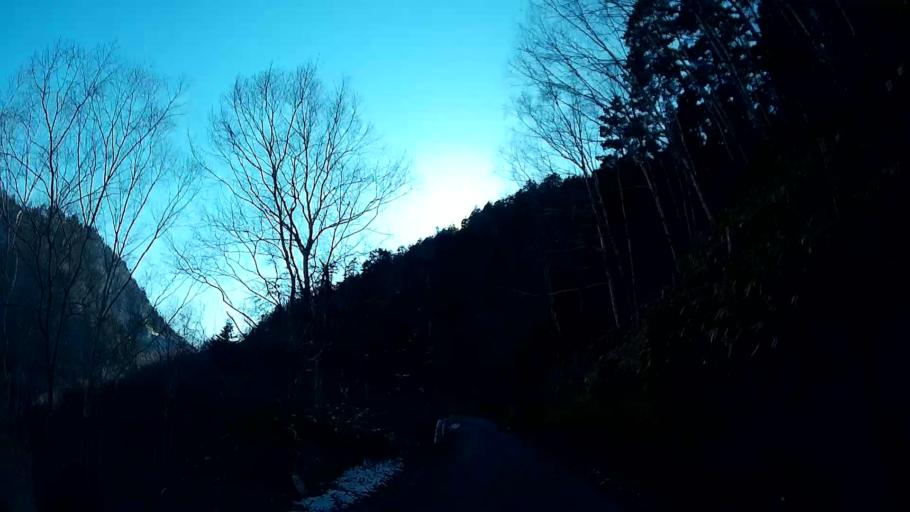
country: JP
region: Nagano
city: Hotaka
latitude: 36.1986
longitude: 137.5861
